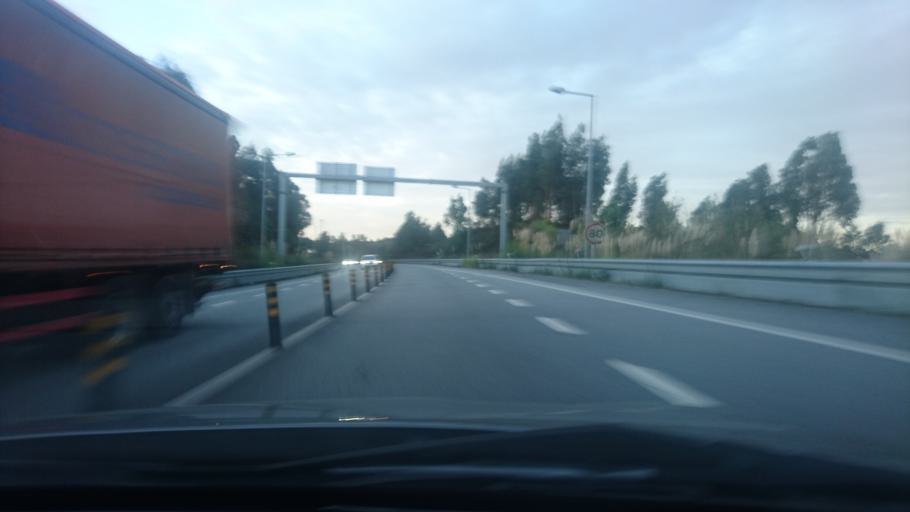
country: PT
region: Aveiro
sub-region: Santa Maria da Feira
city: Arrifana
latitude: 40.9222
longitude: -8.4901
